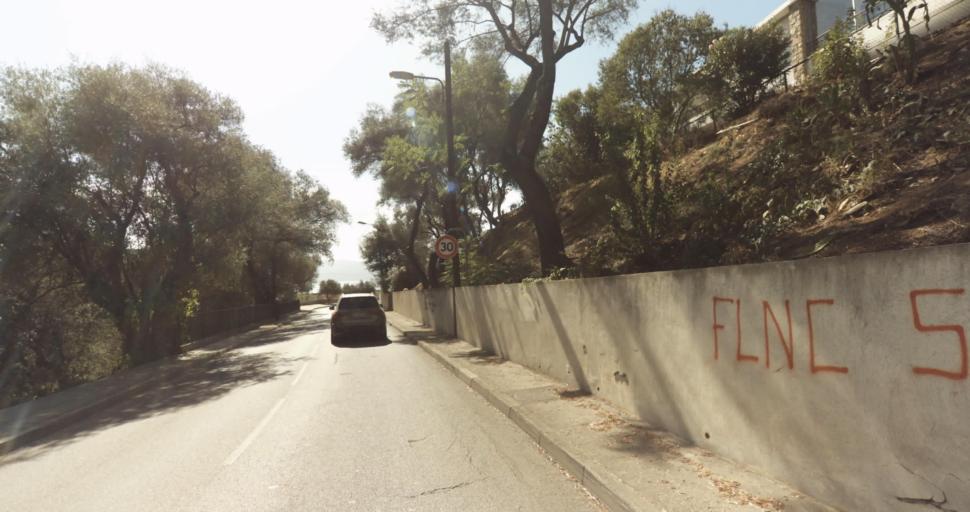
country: FR
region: Corsica
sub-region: Departement de la Corse-du-Sud
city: Ajaccio
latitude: 41.9192
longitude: 8.7264
